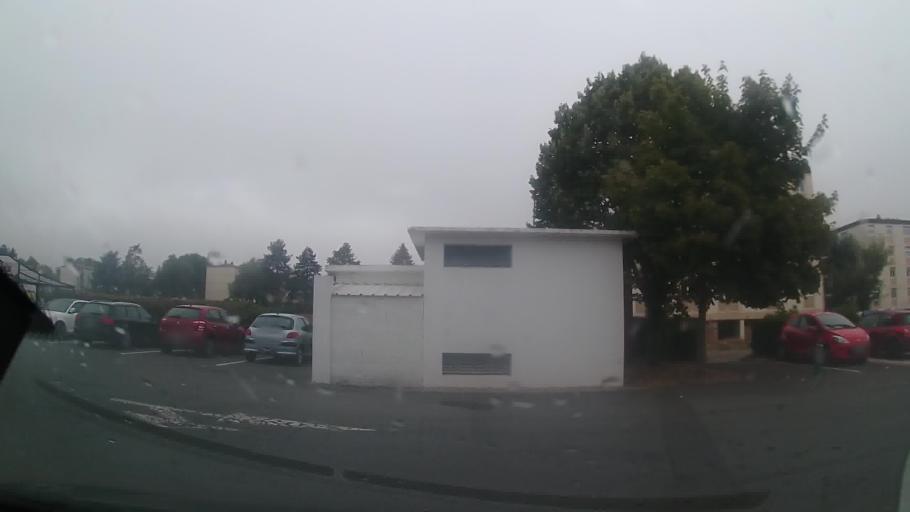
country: FR
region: Ile-de-France
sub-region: Departement de l'Essonne
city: Dourdan
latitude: 48.5277
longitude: 2.0232
